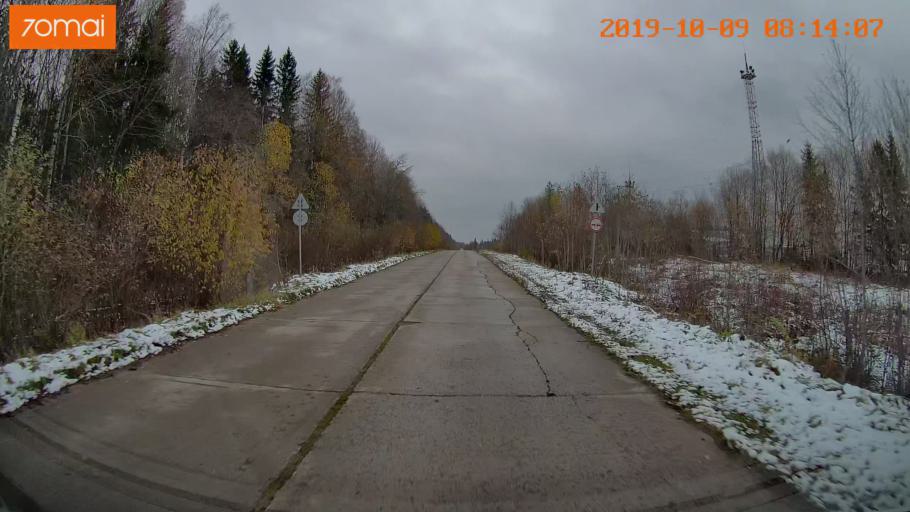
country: RU
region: Vologda
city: Gryazovets
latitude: 58.7270
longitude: 40.1506
